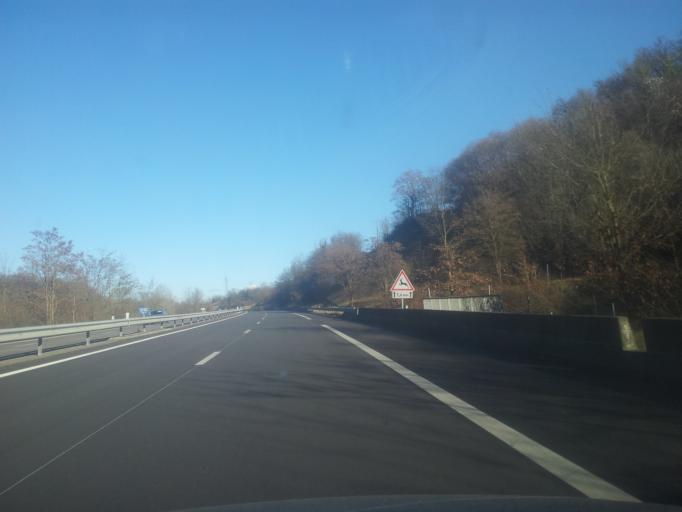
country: FR
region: Rhone-Alpes
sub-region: Departement de l'Isere
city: Saint-Hilaire-du-Rosier
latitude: 45.1045
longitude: 5.2485
